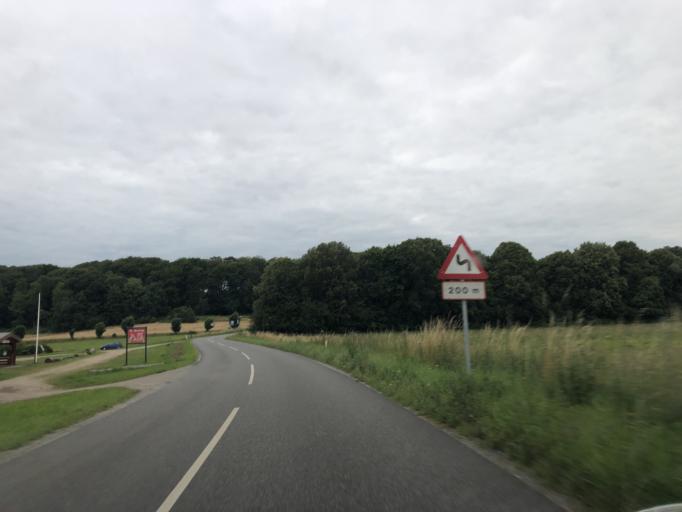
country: DK
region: South Denmark
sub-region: Vejle Kommune
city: Jelling
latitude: 55.7378
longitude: 9.4175
